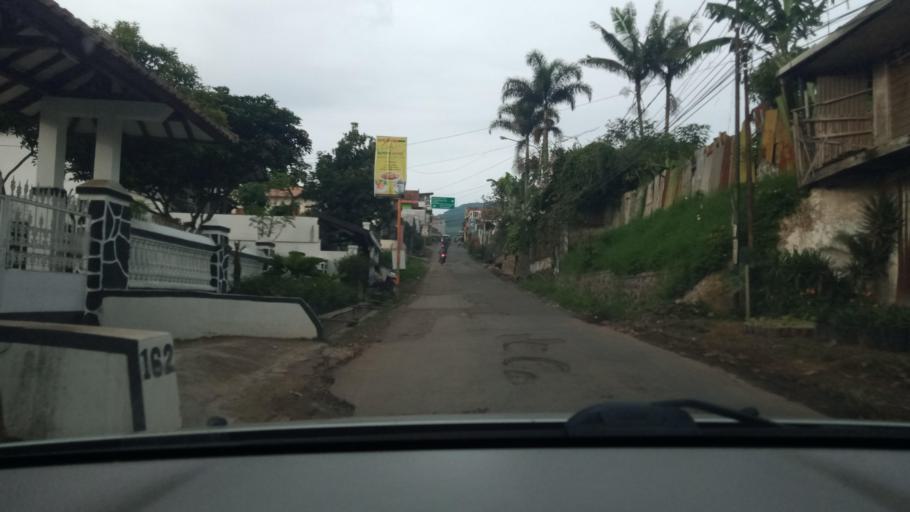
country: ID
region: West Java
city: Lembang
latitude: -6.8066
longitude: 107.5887
